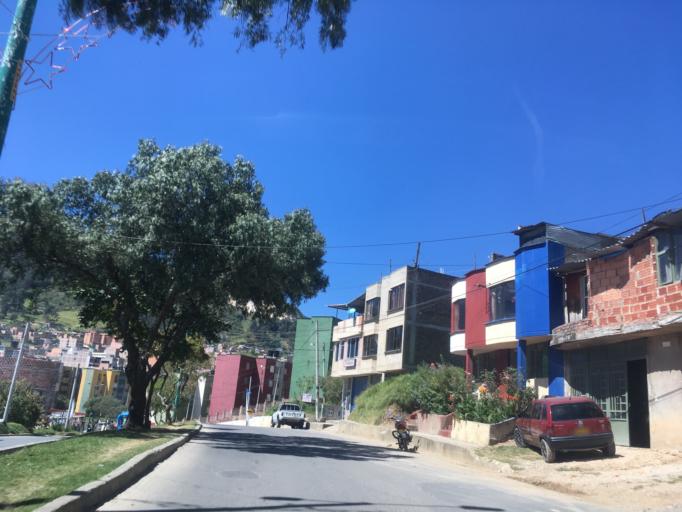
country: CO
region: Boyaca
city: Duitama
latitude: 5.8269
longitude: -73.0419
